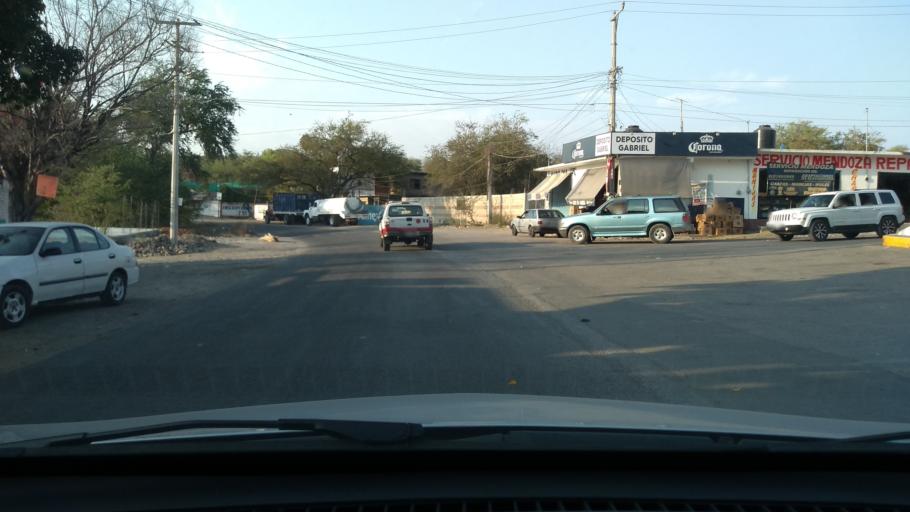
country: MX
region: Morelos
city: Puente de Ixtla
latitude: 18.6135
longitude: -99.3120
